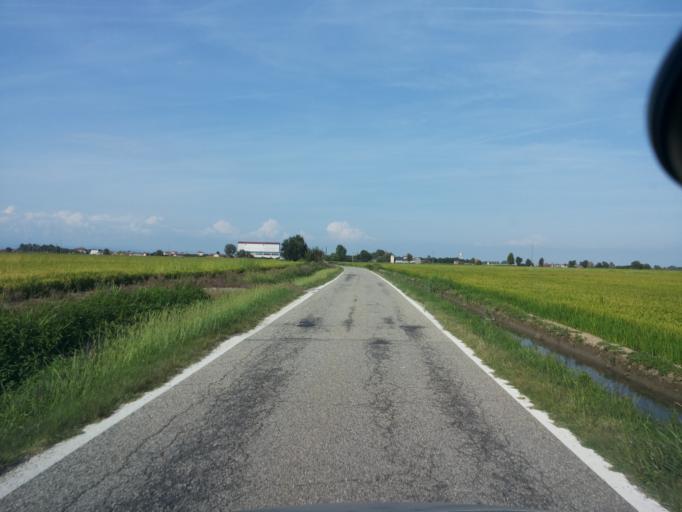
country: IT
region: Piedmont
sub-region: Provincia di Vercelli
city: San Germano Vercellese
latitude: 45.3398
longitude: 8.2379
